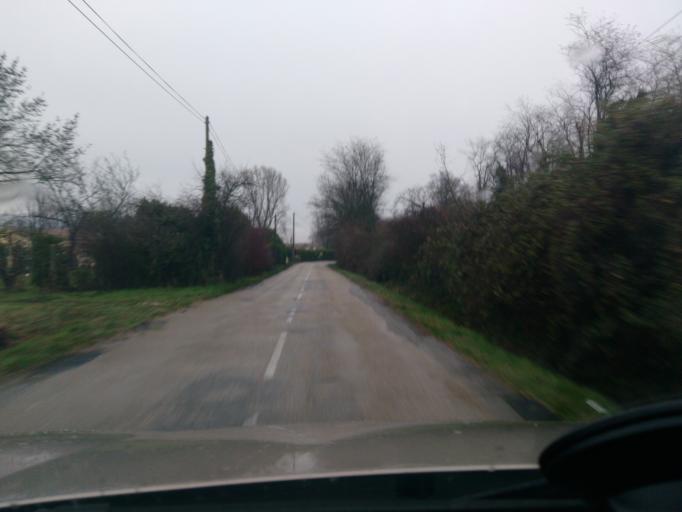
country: FR
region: Rhone-Alpes
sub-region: Departement de la Drome
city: Montelimar
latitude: 44.5375
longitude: 4.7201
